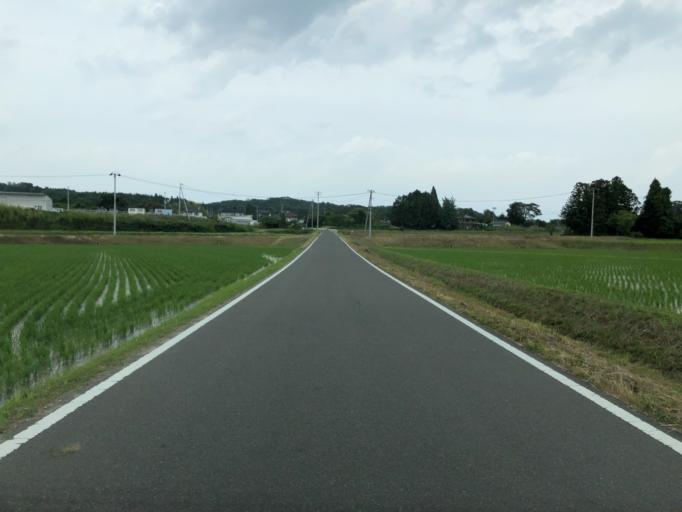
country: JP
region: Miyagi
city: Marumori
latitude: 37.7675
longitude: 140.9360
